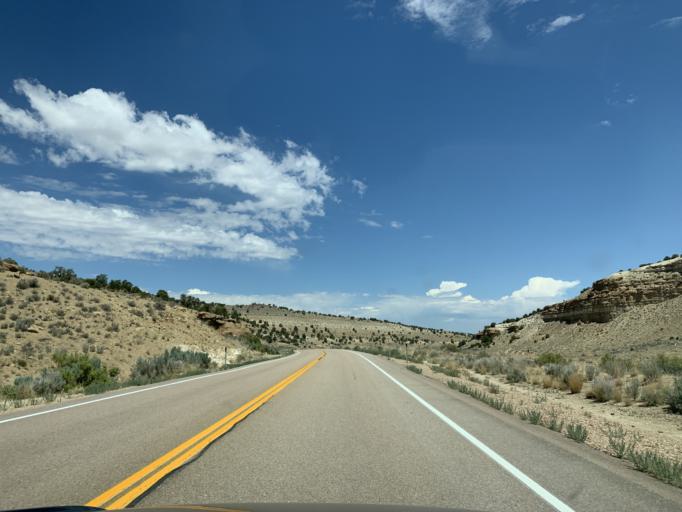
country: US
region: Utah
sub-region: Duchesne County
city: Duchesne
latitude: 39.9815
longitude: -110.1621
